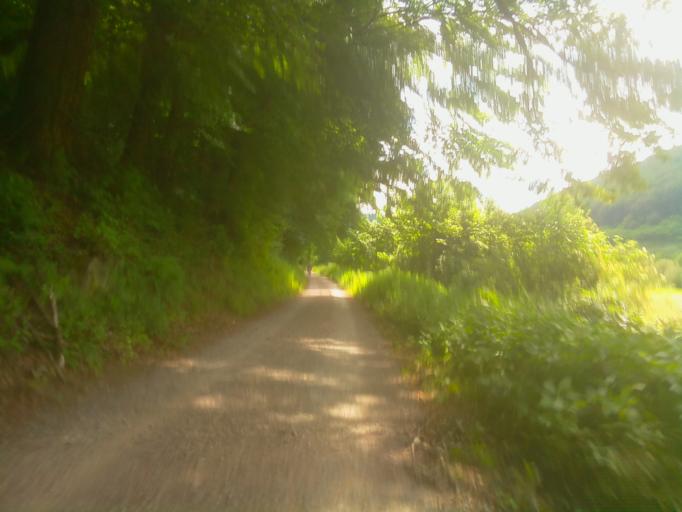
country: DE
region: Hesse
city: Hirschhorn
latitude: 49.4350
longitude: 8.8974
